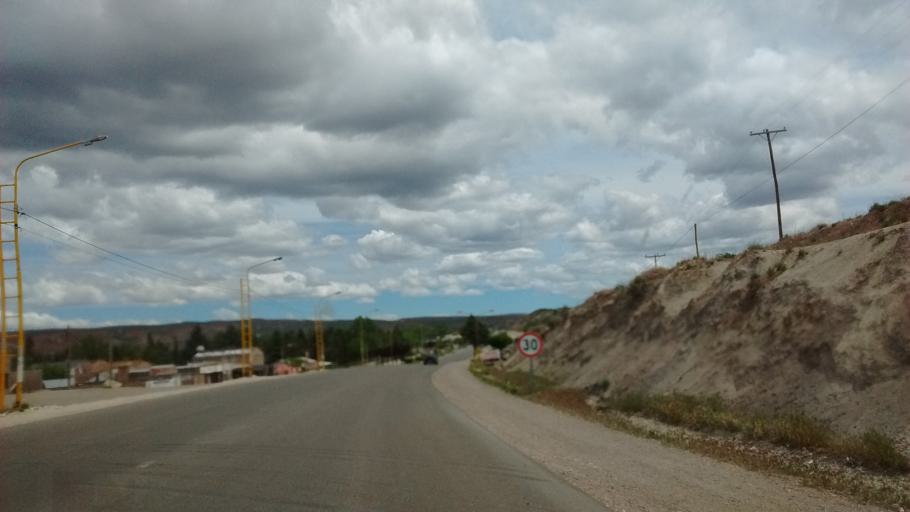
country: AR
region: Neuquen
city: Piedra del Aguila
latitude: -40.0461
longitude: -70.0737
